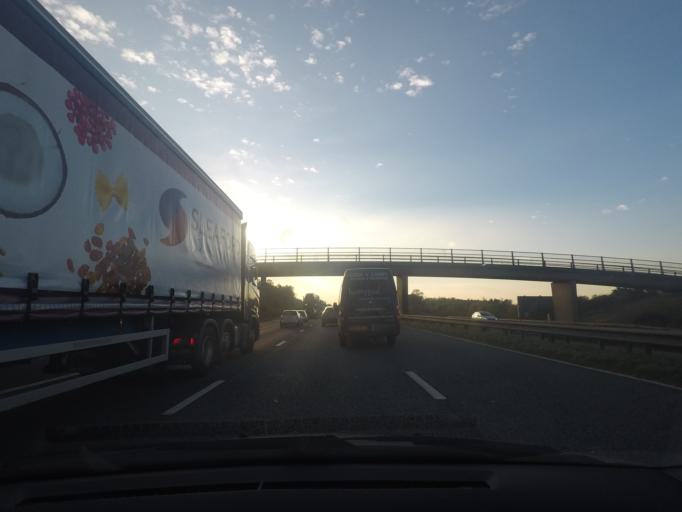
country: GB
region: England
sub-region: North Lincolnshire
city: Barnetby le Wold
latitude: 53.5819
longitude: -0.4356
